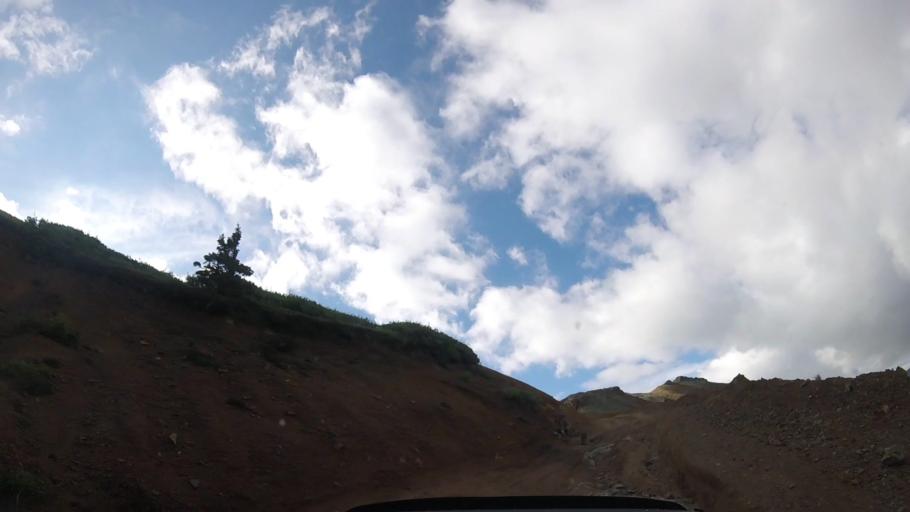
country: US
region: Colorado
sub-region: San Juan County
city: Silverton
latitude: 37.9078
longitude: -107.6634
